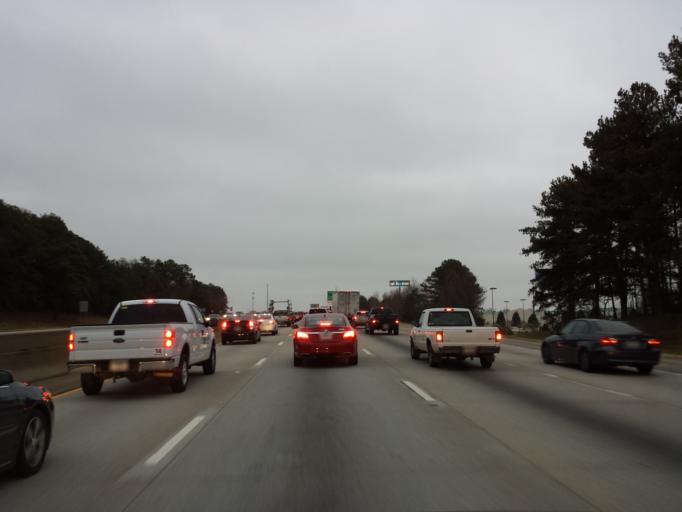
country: US
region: Georgia
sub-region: Henry County
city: Stockbridge
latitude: 33.5496
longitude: -84.2857
